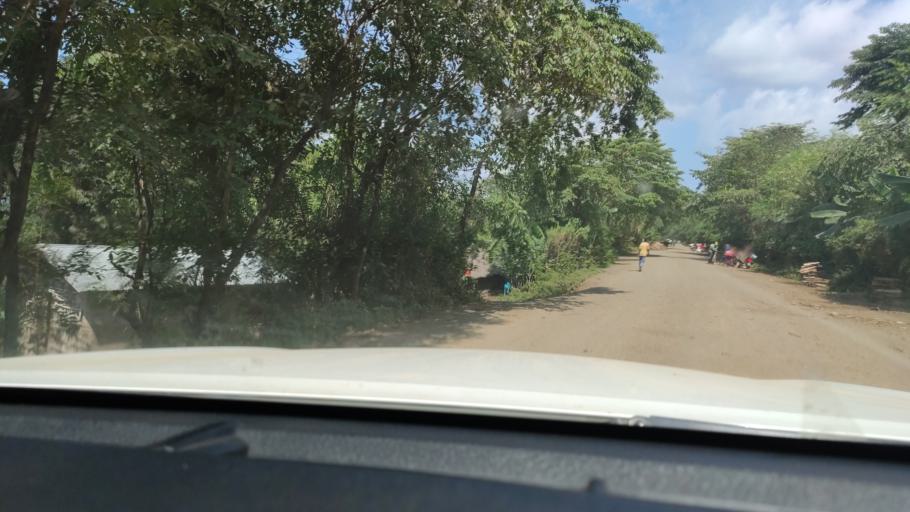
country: ET
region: Southern Nations, Nationalities, and People's Region
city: Felege Neway
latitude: 6.3962
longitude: 37.0795
